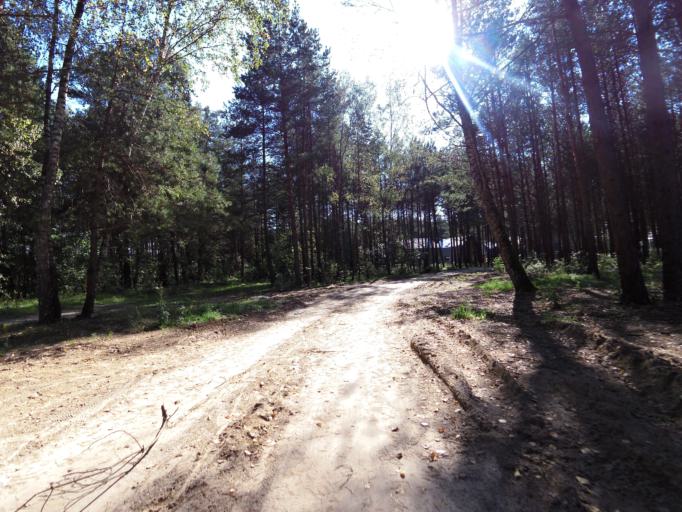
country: LT
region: Vilnius County
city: Lazdynai
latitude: 54.6791
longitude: 25.1927
